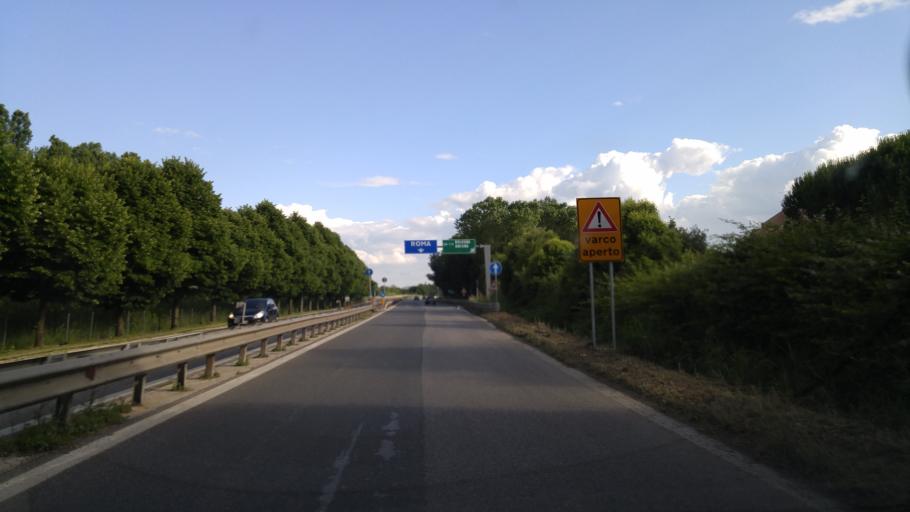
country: IT
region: The Marches
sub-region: Provincia di Pesaro e Urbino
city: Fano
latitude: 43.8281
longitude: 13.0146
